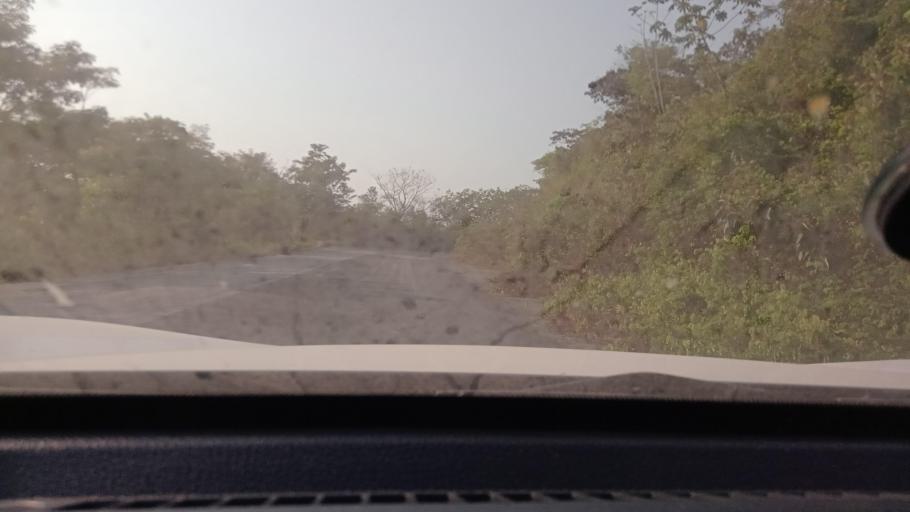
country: MX
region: Tabasco
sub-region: Huimanguillo
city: Francisco Rueda
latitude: 17.6666
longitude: -93.8674
